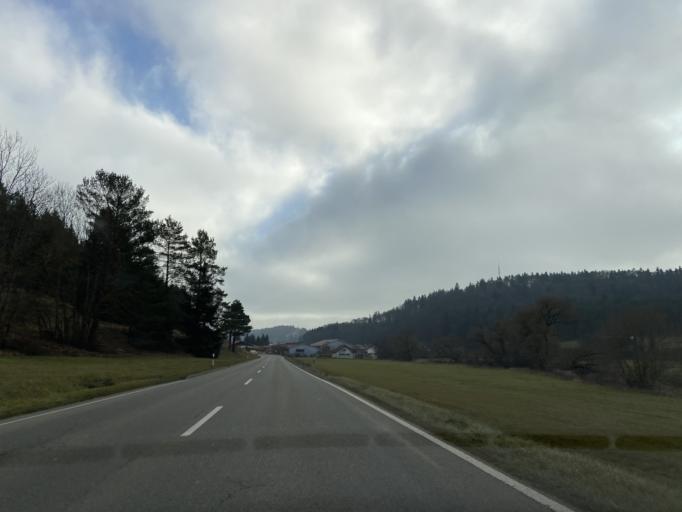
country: DE
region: Baden-Wuerttemberg
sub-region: Tuebingen Region
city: Neufra
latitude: 48.2569
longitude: 9.1745
